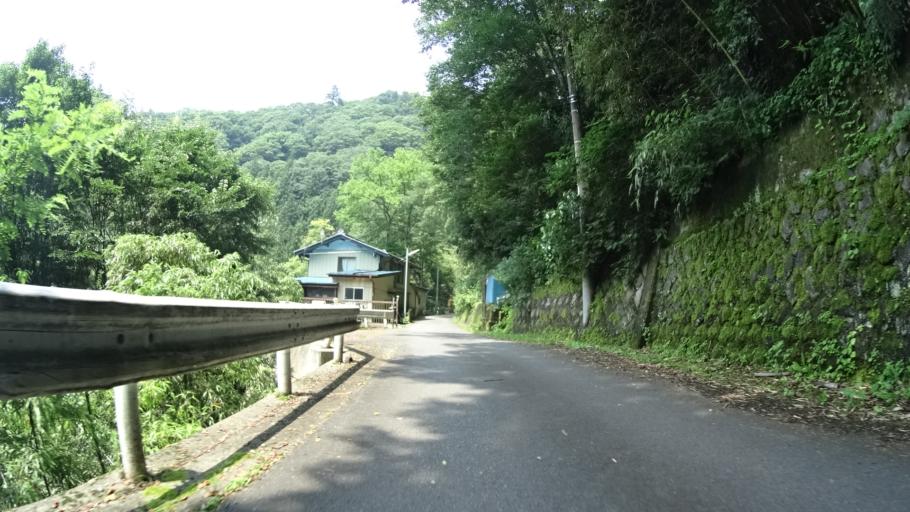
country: JP
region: Gunma
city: Tomioka
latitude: 36.0832
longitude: 138.7169
